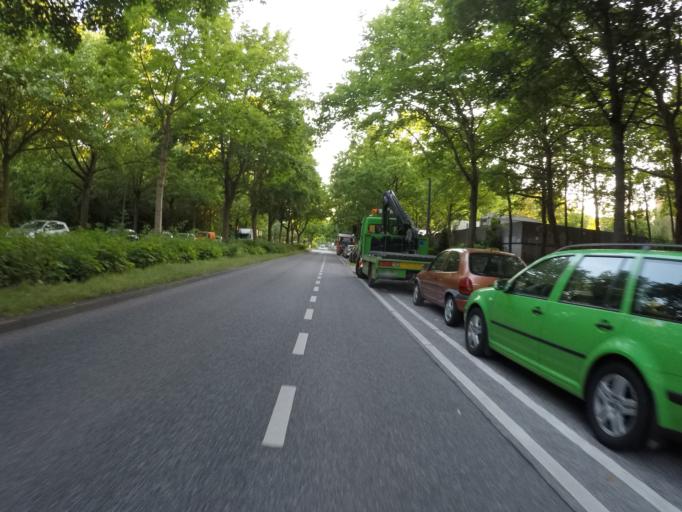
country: DE
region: Hamburg
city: Steilshoop
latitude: 53.6132
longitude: 10.0652
